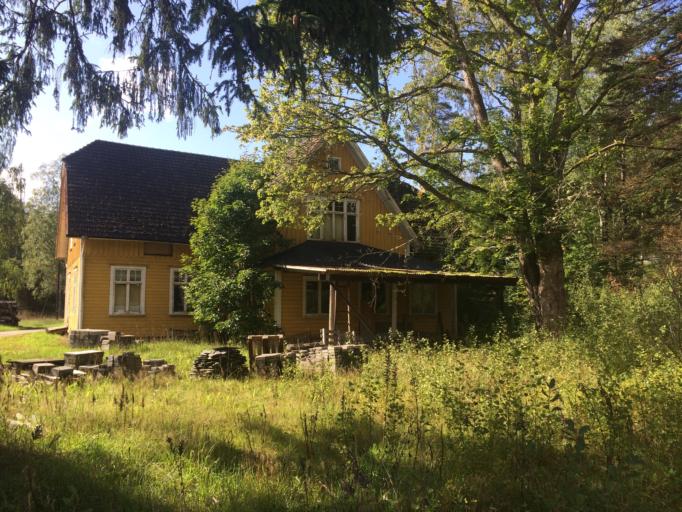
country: SE
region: Vaestra Goetaland
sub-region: Svenljunga Kommun
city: Svenljunga
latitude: 57.4648
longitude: 13.2076
